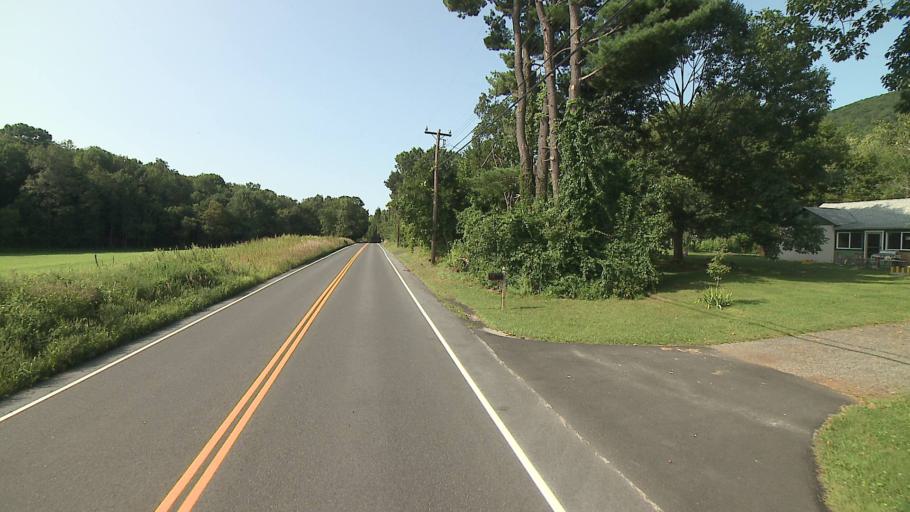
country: US
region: Connecticut
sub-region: Litchfield County
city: Kent
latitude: 41.7013
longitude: -73.4924
